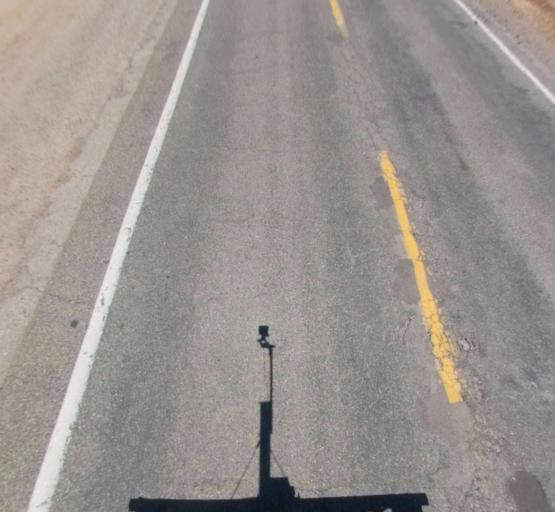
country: US
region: California
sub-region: Madera County
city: Fairmead
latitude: 37.0485
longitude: -120.2568
